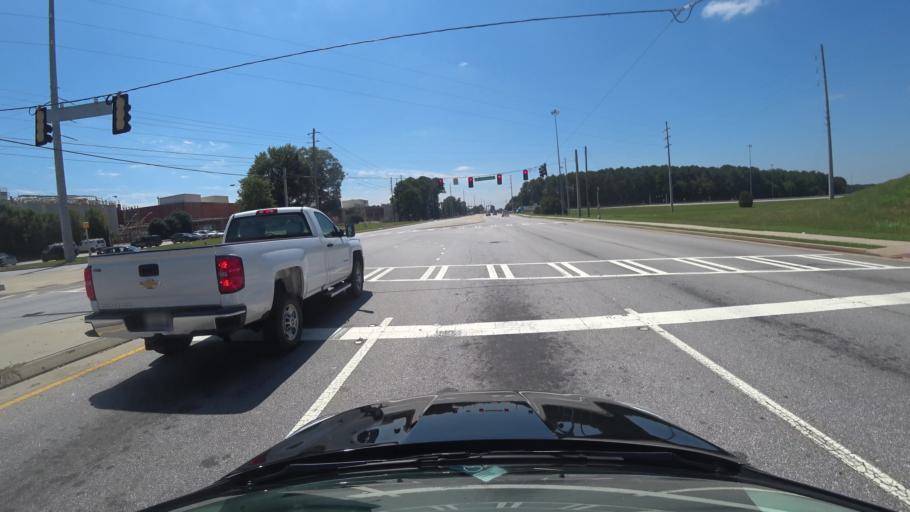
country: US
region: Georgia
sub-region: Newton County
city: Oxford
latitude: 33.6152
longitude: -83.8454
